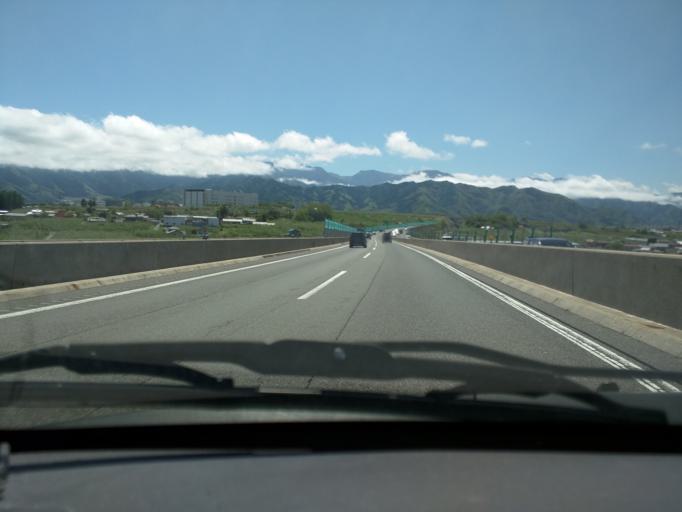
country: JP
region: Nagano
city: Nakano
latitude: 36.7438
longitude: 138.3134
